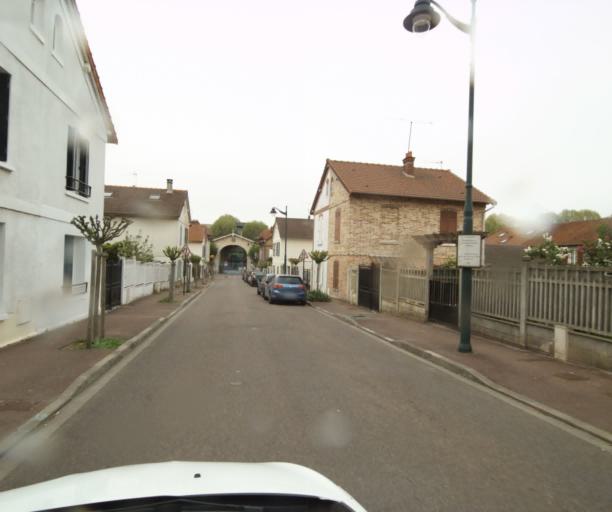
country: FR
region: Ile-de-France
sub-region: Departement de Seine-et-Marne
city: Noisiel
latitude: 48.8554
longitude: 2.6276
